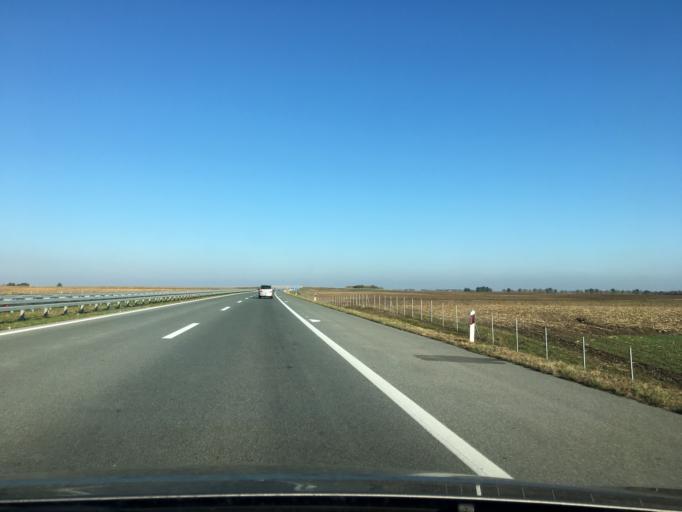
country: RS
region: Autonomna Pokrajina Vojvodina
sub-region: Severnobacki Okrug
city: Mali Igos
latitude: 45.7386
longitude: 19.7035
